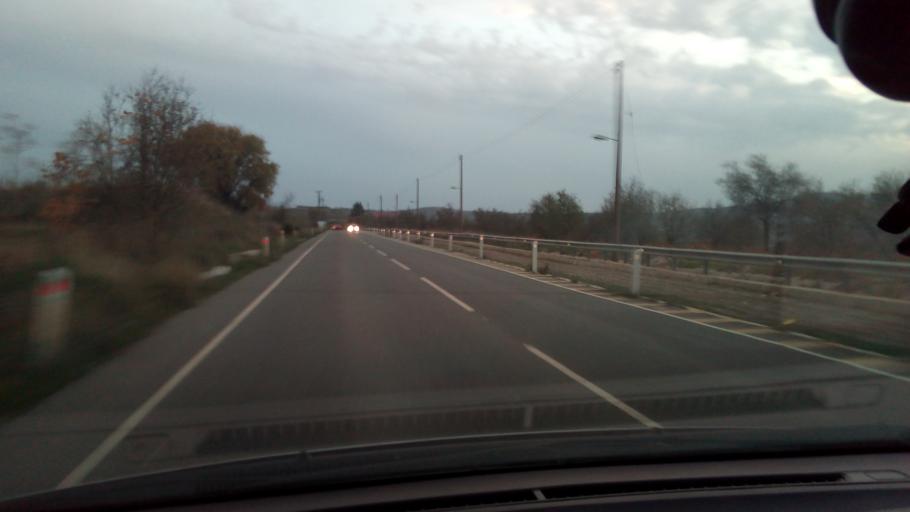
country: CY
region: Pafos
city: Tala
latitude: 34.9152
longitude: 32.4679
